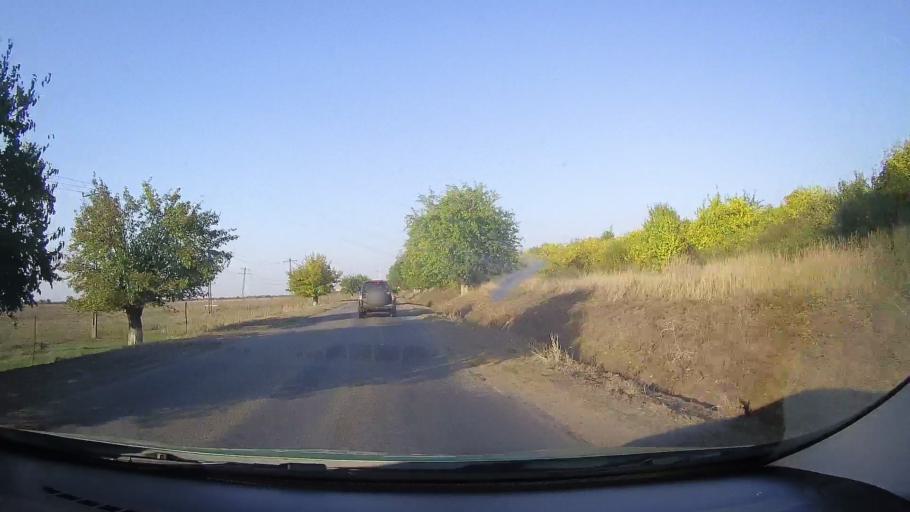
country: RO
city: Masca
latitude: 46.3059
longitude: 21.6745
